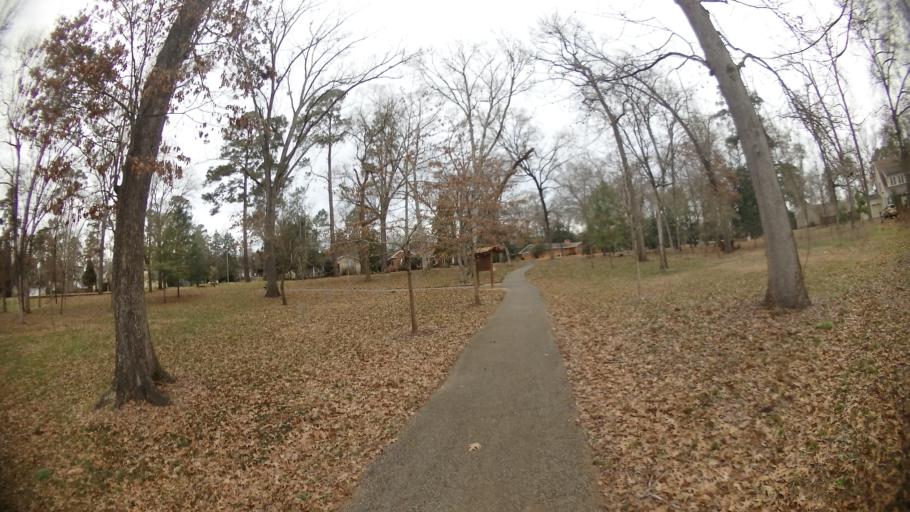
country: US
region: Texas
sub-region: Nacogdoches County
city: Nacogdoches
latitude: 31.6306
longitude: -94.6474
